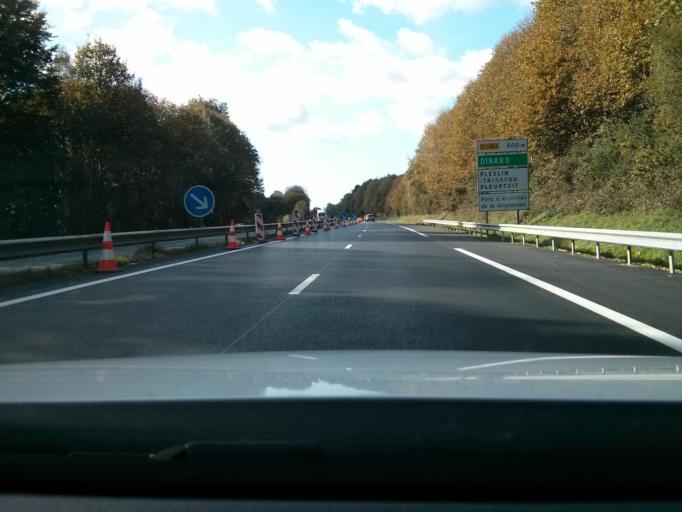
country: FR
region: Brittany
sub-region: Departement des Cotes-d'Armor
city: Plouer-sur-Rance
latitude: 48.5291
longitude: -2.0301
